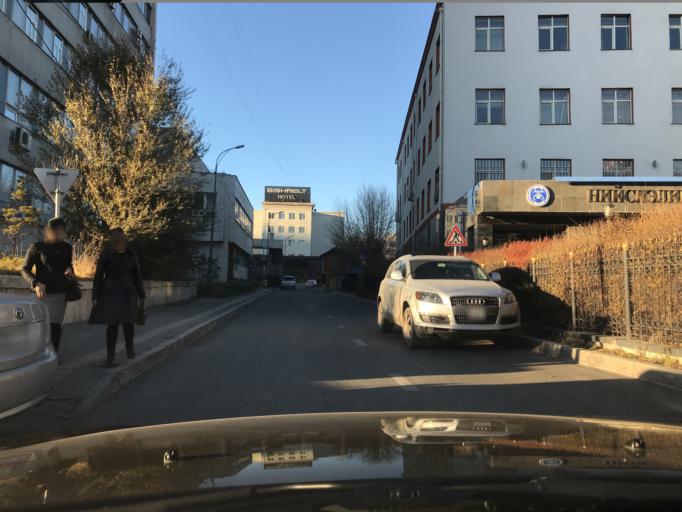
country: MN
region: Ulaanbaatar
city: Ulaanbaatar
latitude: 47.9223
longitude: 106.9073
